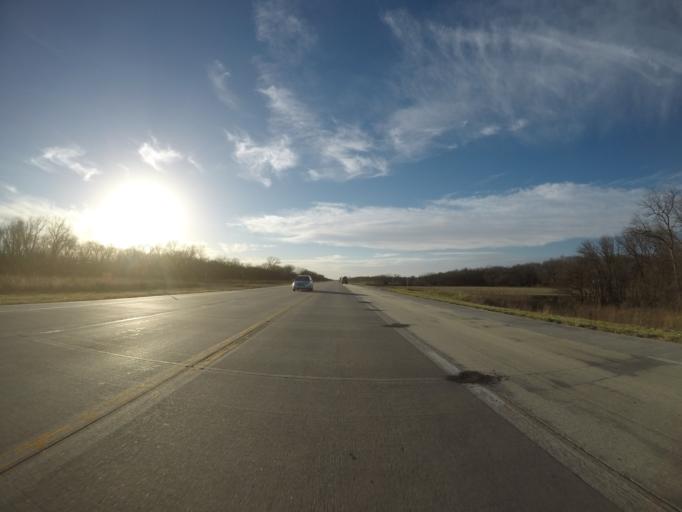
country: US
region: Kansas
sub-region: Lyon County
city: Emporia
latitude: 38.4065
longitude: -96.3266
